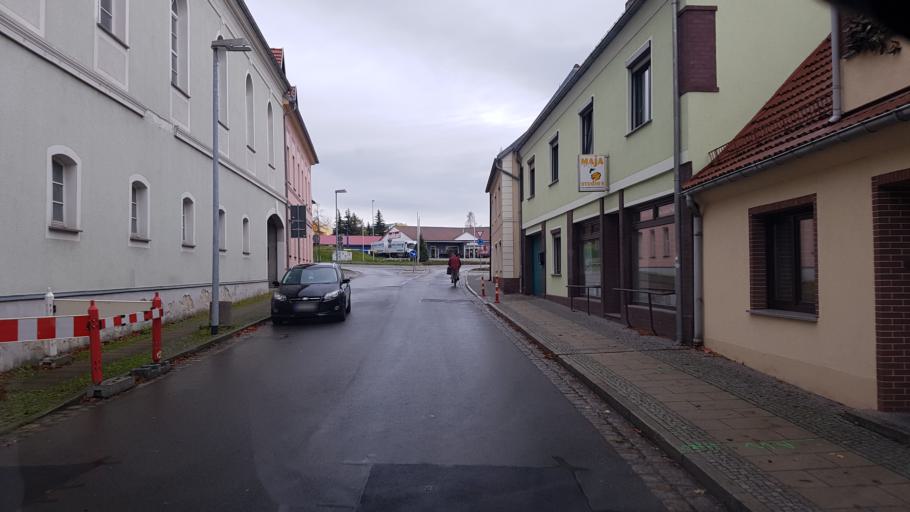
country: DE
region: Brandenburg
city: Ortrand
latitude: 51.3746
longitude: 13.7596
